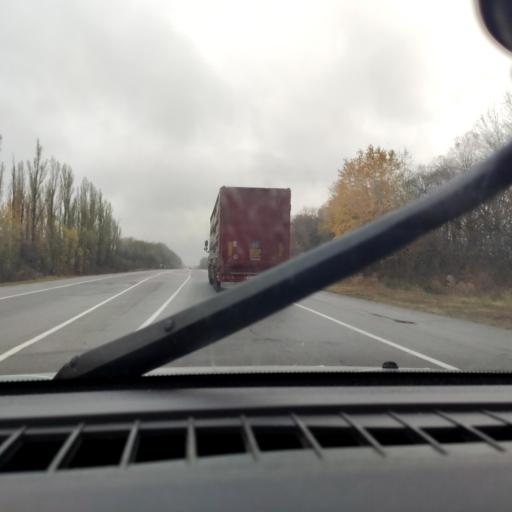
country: RU
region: Voronezj
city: Kolodeznyy
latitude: 51.2666
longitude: 39.0504
